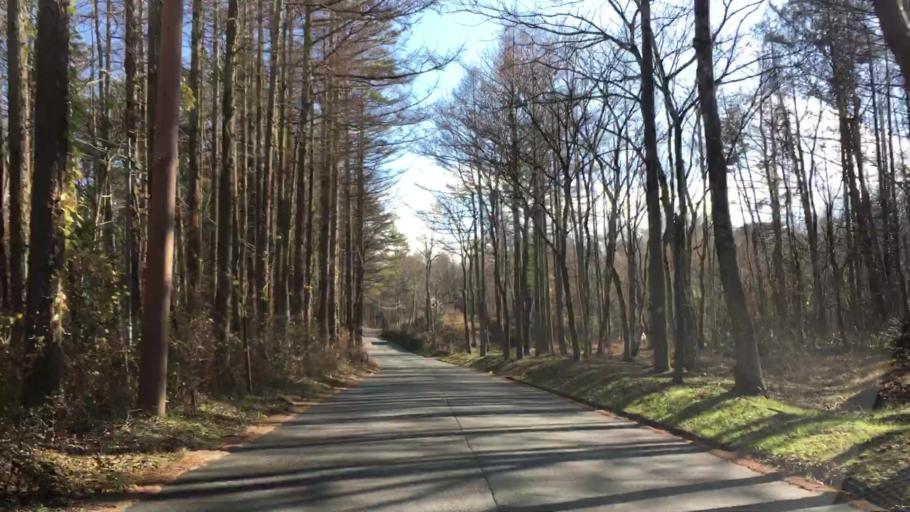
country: JP
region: Shizuoka
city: Gotemba
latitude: 35.4082
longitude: 138.8621
